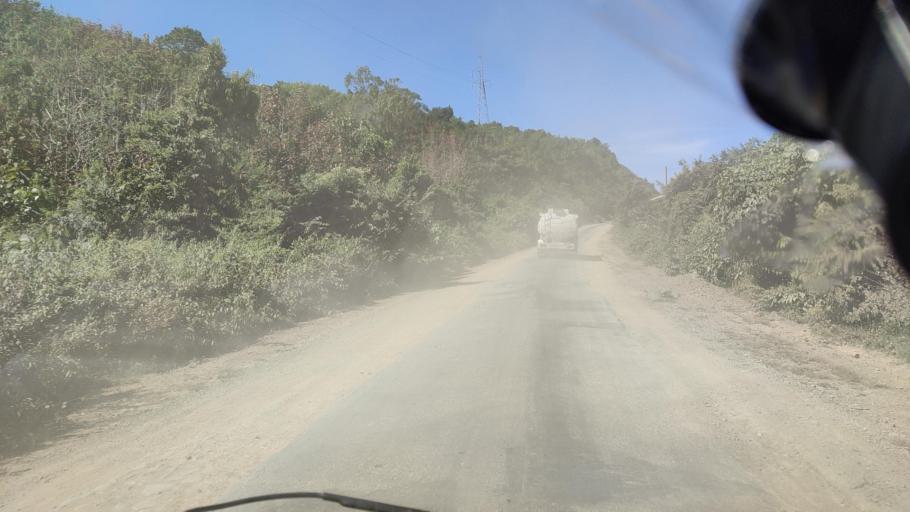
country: MM
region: Rakhine
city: Sittwe
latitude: 20.0076
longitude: 93.5860
